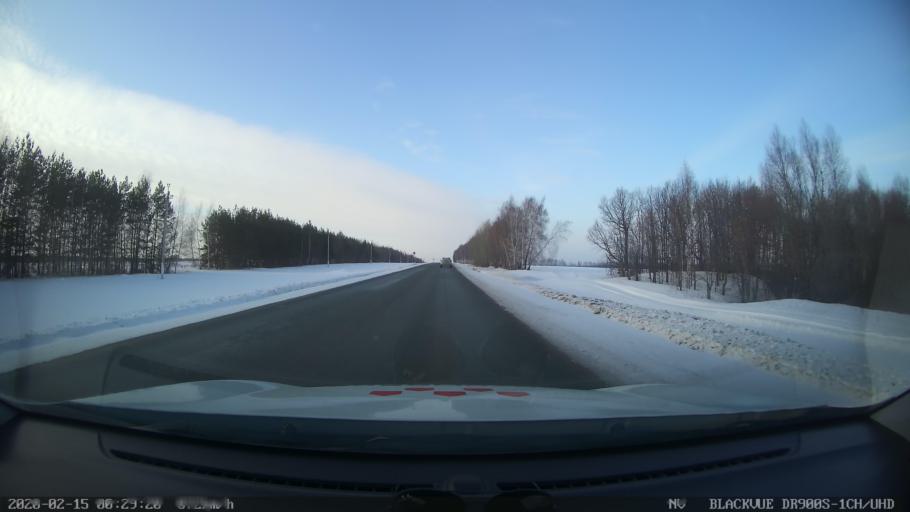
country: RU
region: Tatarstan
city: Verkhniy Uslon
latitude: 55.6498
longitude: 48.8695
